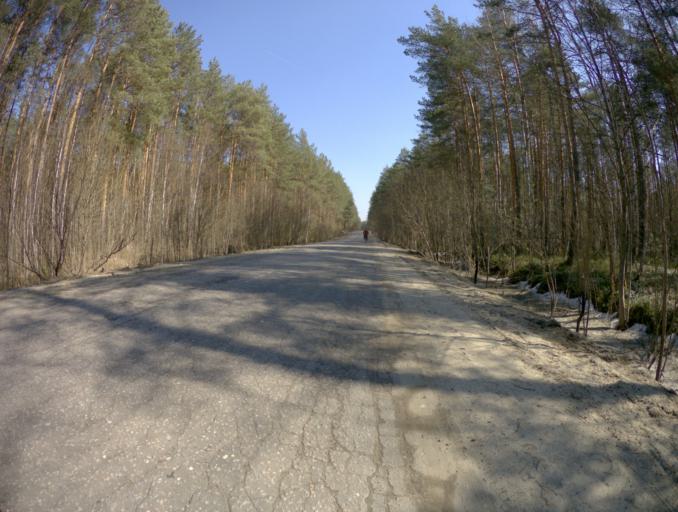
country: RU
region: Vladimir
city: Bogolyubovo
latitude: 56.1447
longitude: 40.5155
